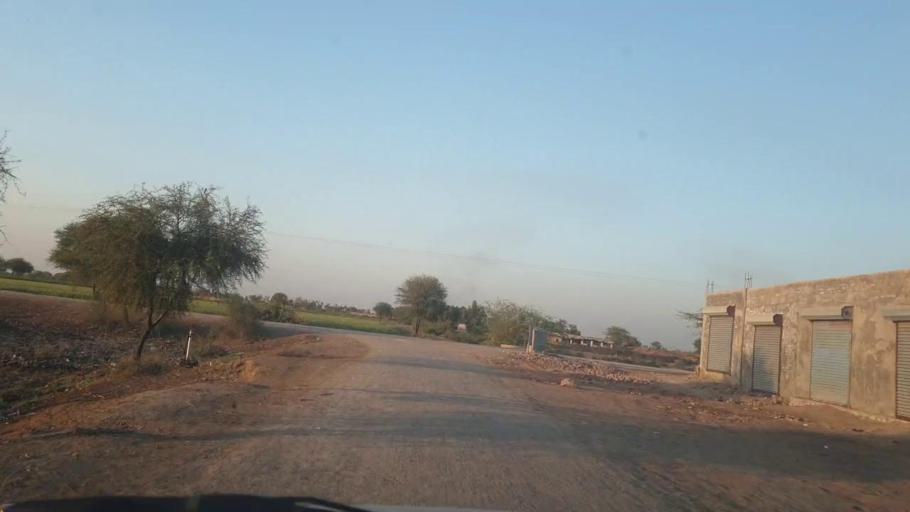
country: PK
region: Sindh
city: Mirpur Khas
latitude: 25.4691
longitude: 69.0701
